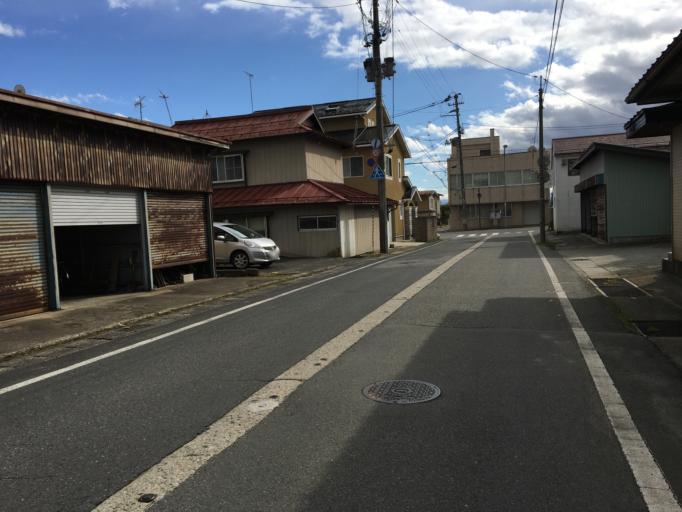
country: JP
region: Yamagata
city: Nagai
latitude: 38.1074
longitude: 140.0344
